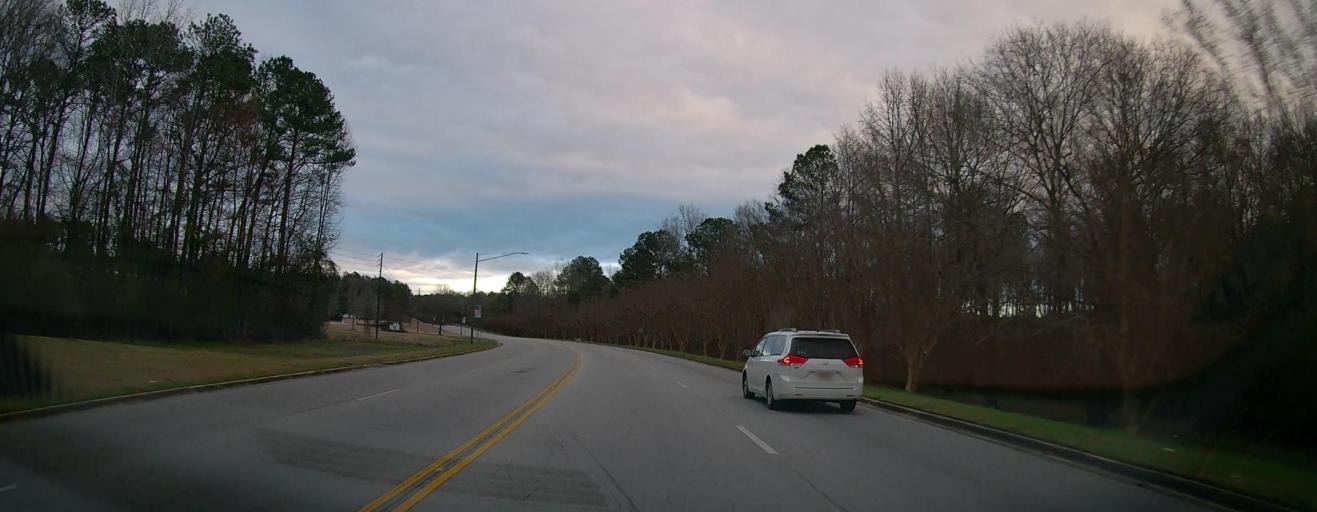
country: US
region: Alabama
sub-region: Chambers County
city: Valley
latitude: 32.8150
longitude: -85.1860
